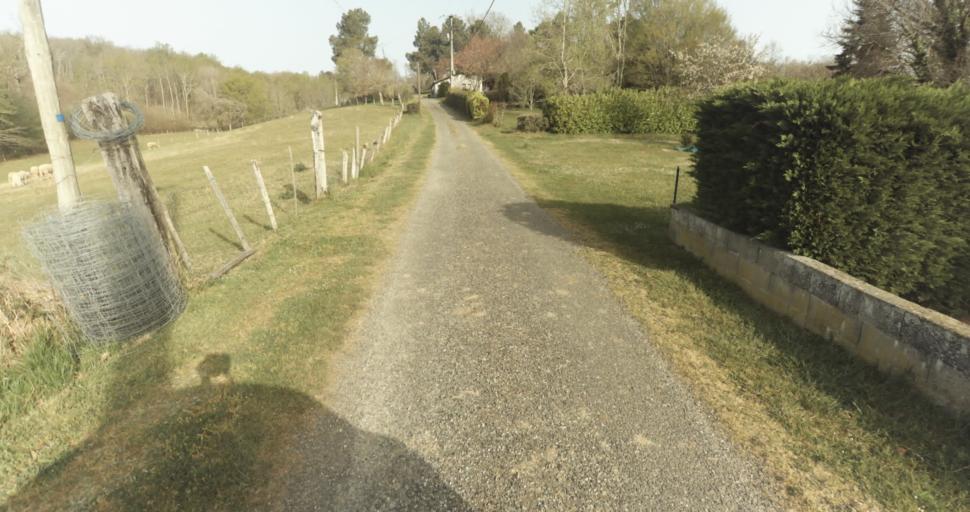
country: FR
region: Midi-Pyrenees
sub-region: Departement du Tarn-et-Garonne
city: Moissac
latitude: 44.1509
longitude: 1.1050
